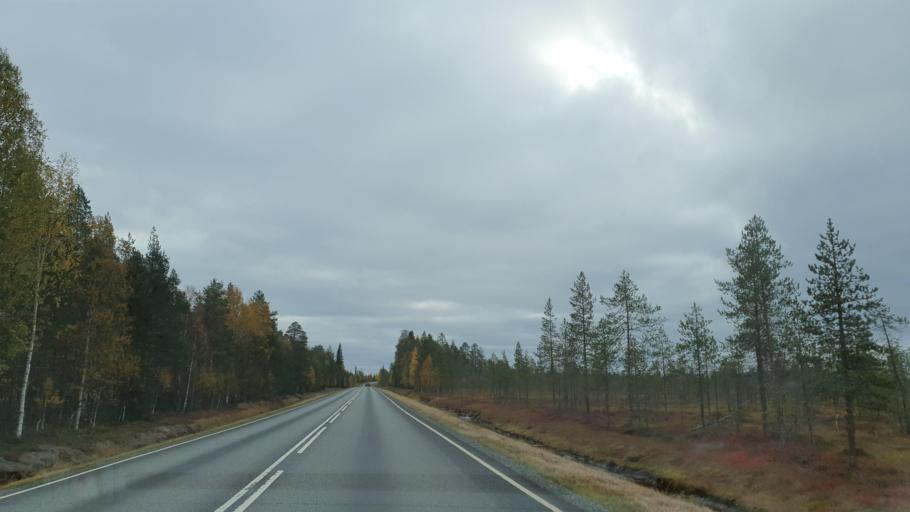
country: FI
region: Lapland
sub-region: Rovaniemi
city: Ranua
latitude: 65.8083
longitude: 26.5580
